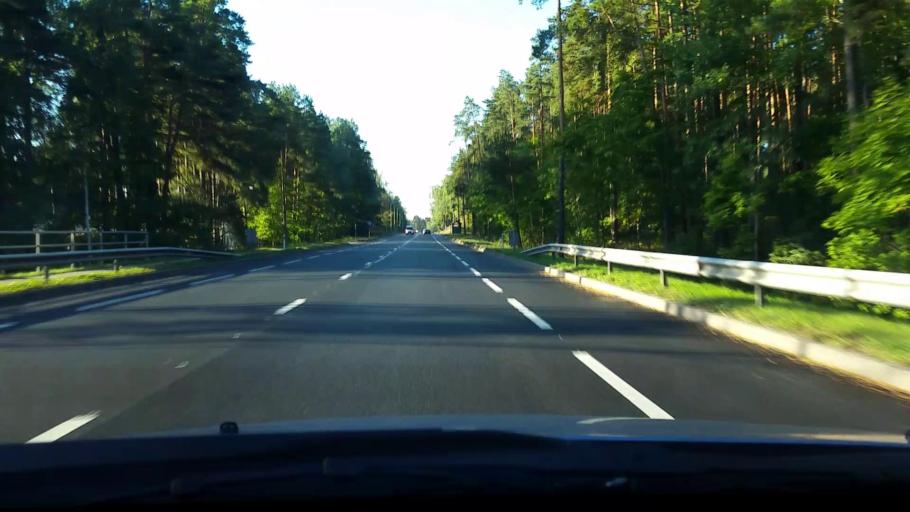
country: LV
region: Adazi
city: Adazi
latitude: 57.0494
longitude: 24.3179
